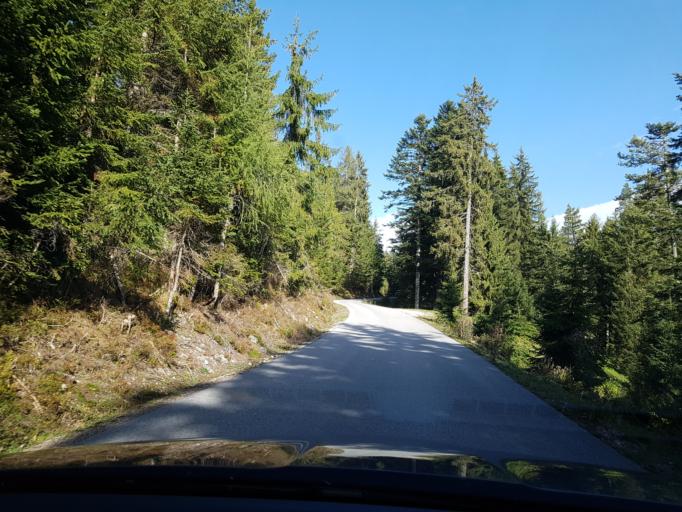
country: AT
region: Salzburg
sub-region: Politischer Bezirk Sankt Johann im Pongau
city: Filzmoos
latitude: 47.4071
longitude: 13.5073
